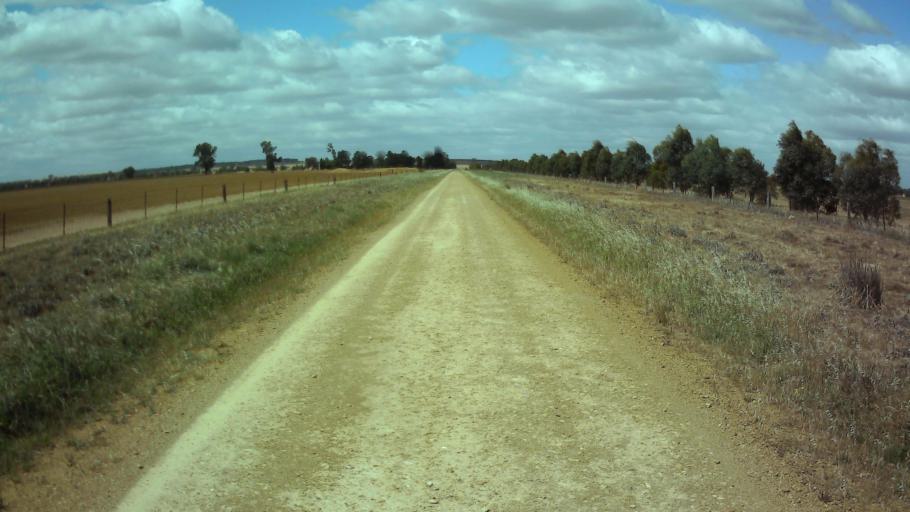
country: AU
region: New South Wales
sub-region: Weddin
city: Grenfell
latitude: -34.0535
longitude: 148.3316
